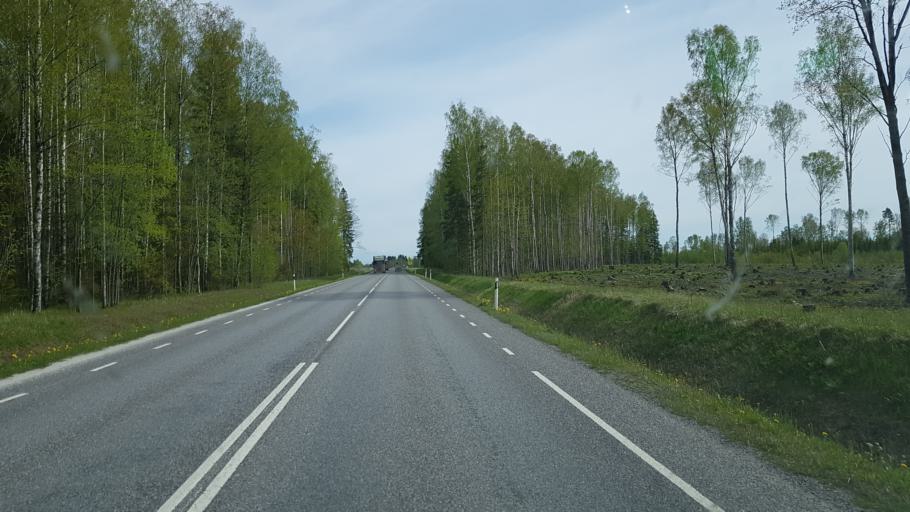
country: EE
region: Ida-Virumaa
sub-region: Johvi vald
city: Johvi
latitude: 59.3235
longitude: 27.4875
